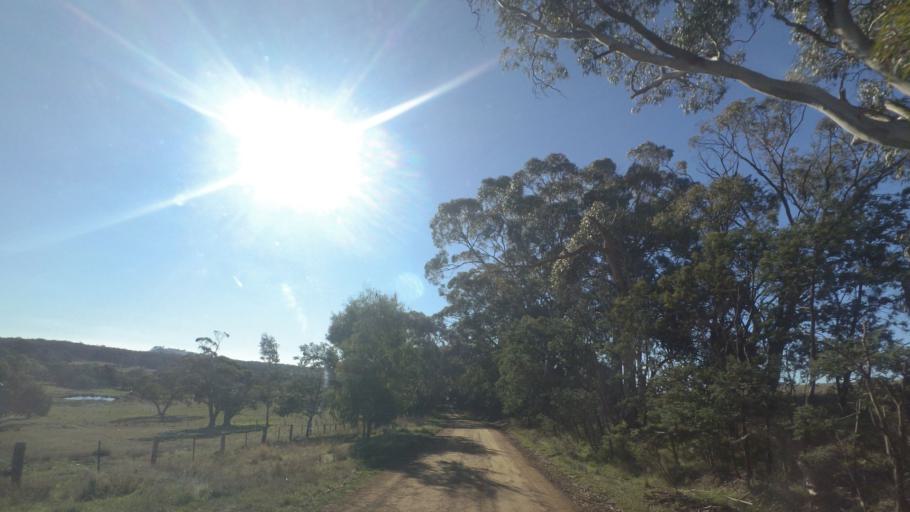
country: AU
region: Victoria
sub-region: Mount Alexander
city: Castlemaine
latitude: -37.2998
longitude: 144.3335
